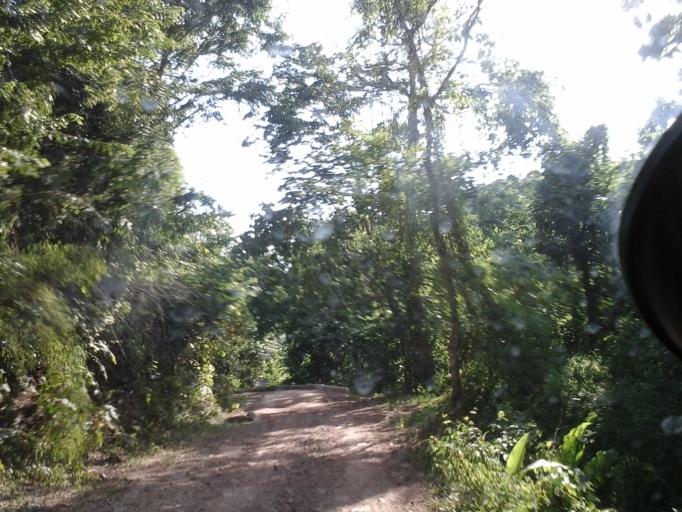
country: CO
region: Cesar
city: San Diego
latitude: 10.2456
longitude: -73.1267
